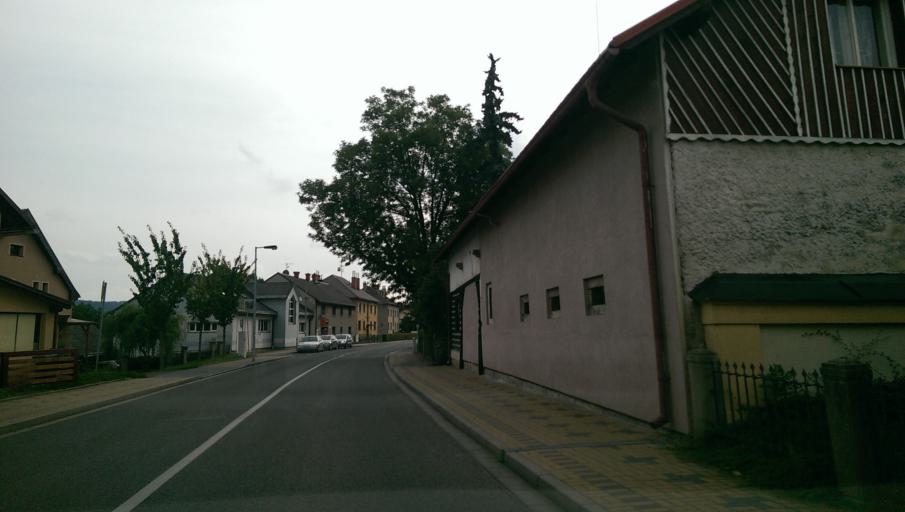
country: CZ
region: Liberecky
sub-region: Okres Semily
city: Turnov
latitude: 50.5930
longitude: 15.1521
